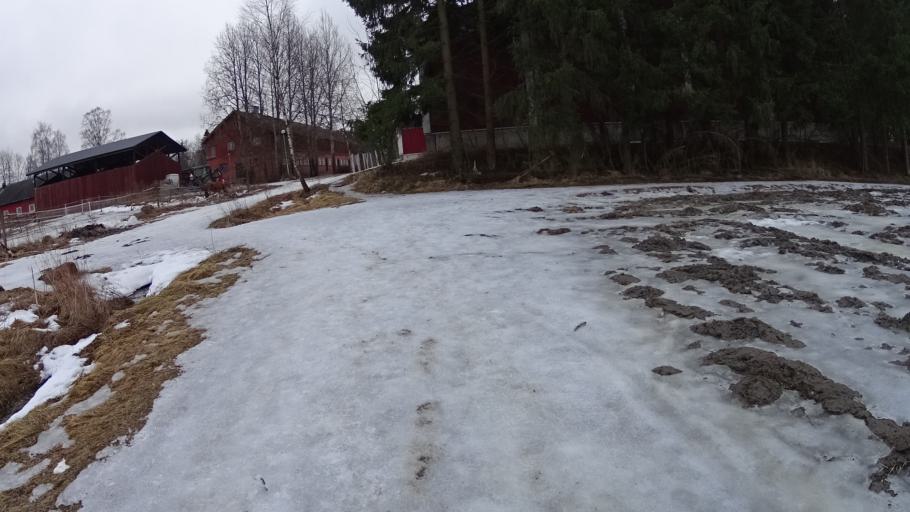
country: FI
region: Uusimaa
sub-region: Helsinki
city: Kilo
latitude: 60.2372
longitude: 24.7833
